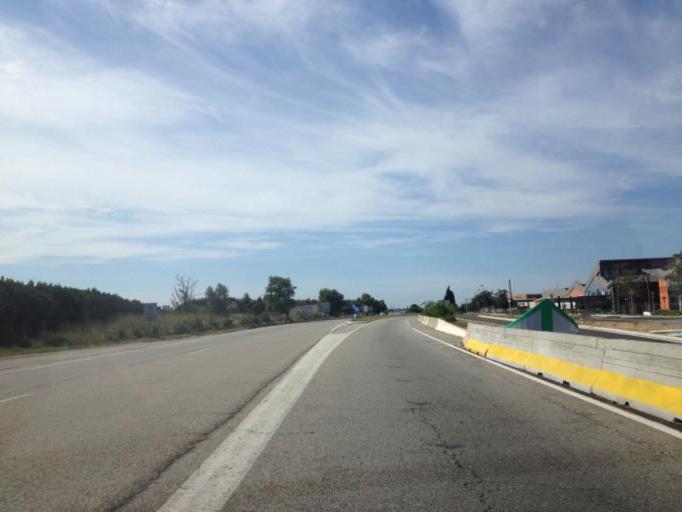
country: FR
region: Provence-Alpes-Cote d'Azur
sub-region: Departement du Vaucluse
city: Courthezon
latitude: 44.1083
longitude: 4.8522
